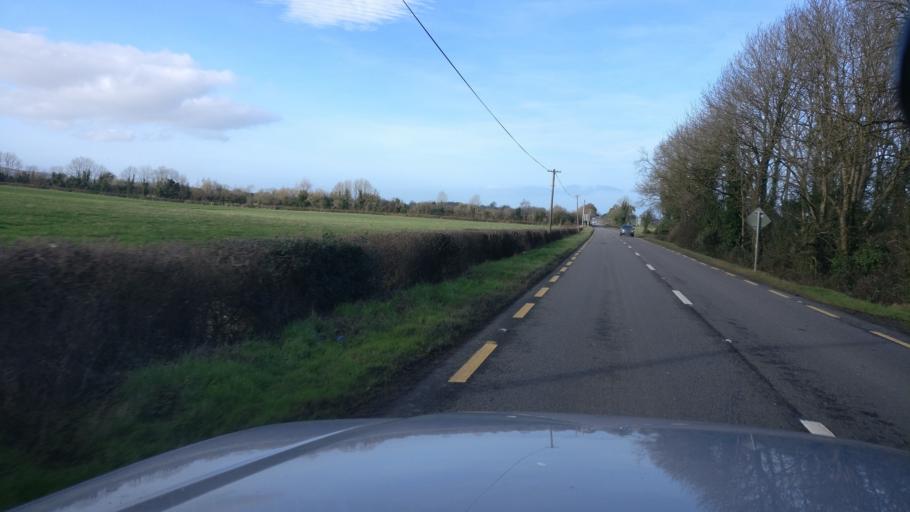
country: IE
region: Leinster
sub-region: Laois
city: Mountmellick
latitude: 53.0855
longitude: -7.3332
